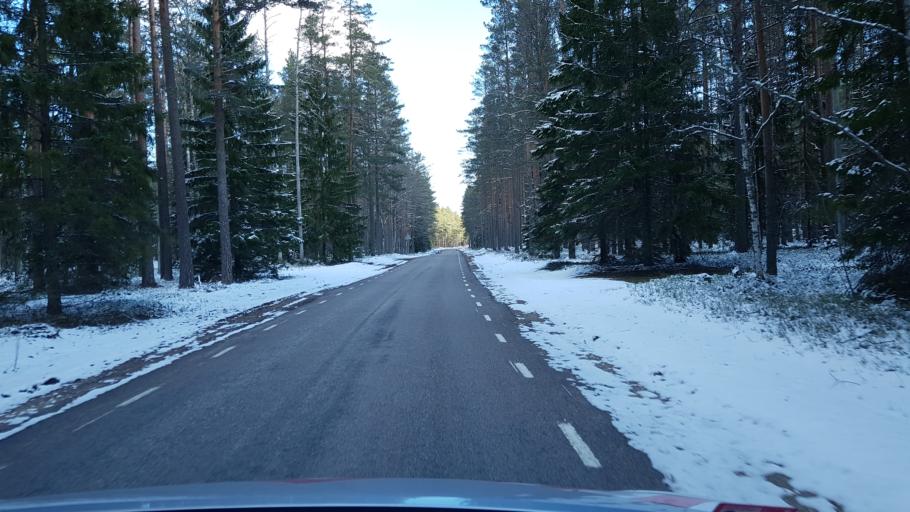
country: EE
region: Harju
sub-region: Loksa linn
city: Loksa
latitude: 59.5379
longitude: 25.9786
